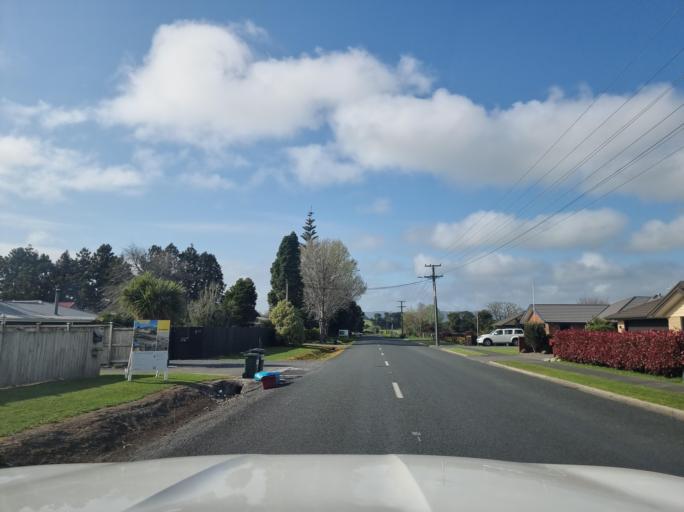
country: NZ
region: Northland
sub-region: Whangarei
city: Ruakaka
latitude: -35.9874
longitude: 174.4489
